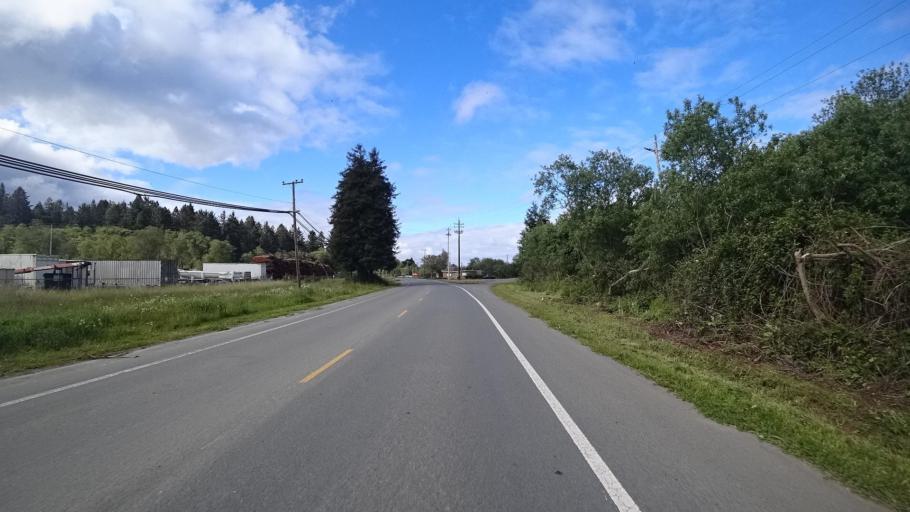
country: US
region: California
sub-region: Humboldt County
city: Arcata
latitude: 40.8953
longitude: -124.0777
